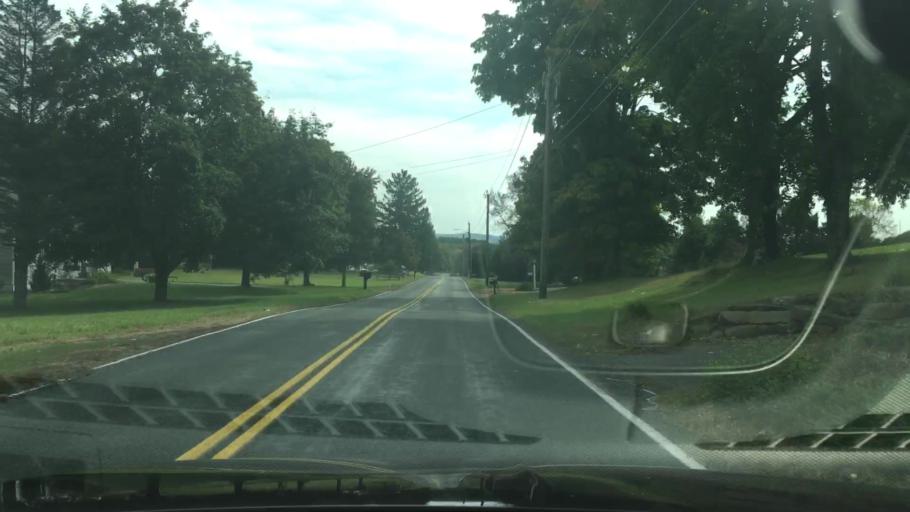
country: US
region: Connecticut
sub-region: Hartford County
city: Hazardville
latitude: 41.9969
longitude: -72.5006
